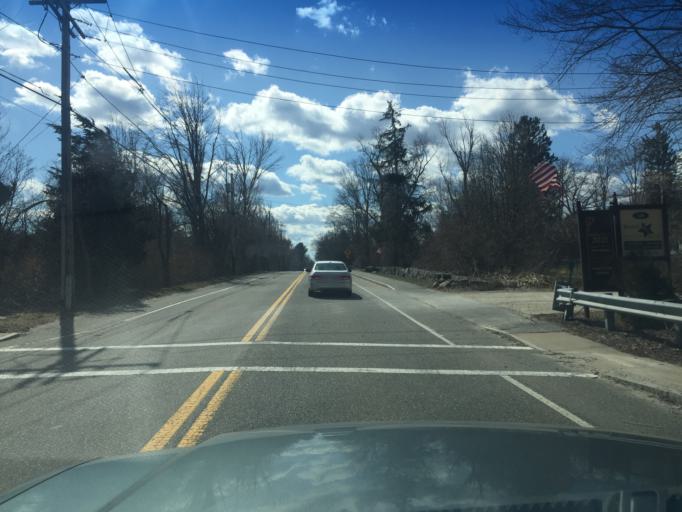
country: US
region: Massachusetts
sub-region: Middlesex County
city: Holliston
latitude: 42.1693
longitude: -71.4438
